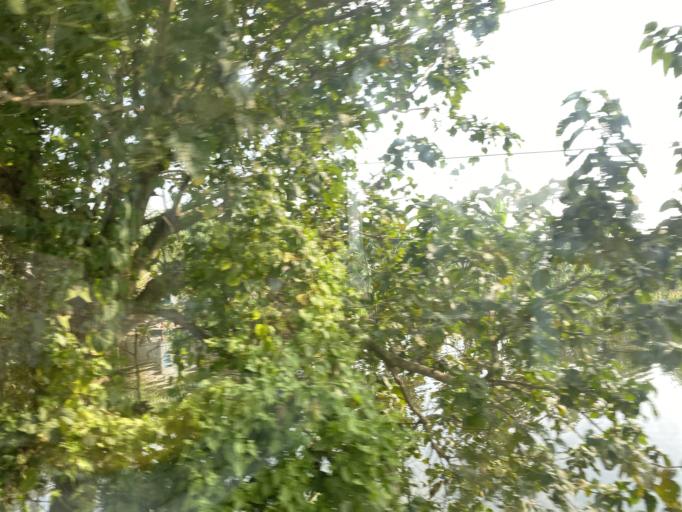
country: BD
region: Chittagong
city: Nabinagar
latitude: 23.9520
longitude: 91.1198
